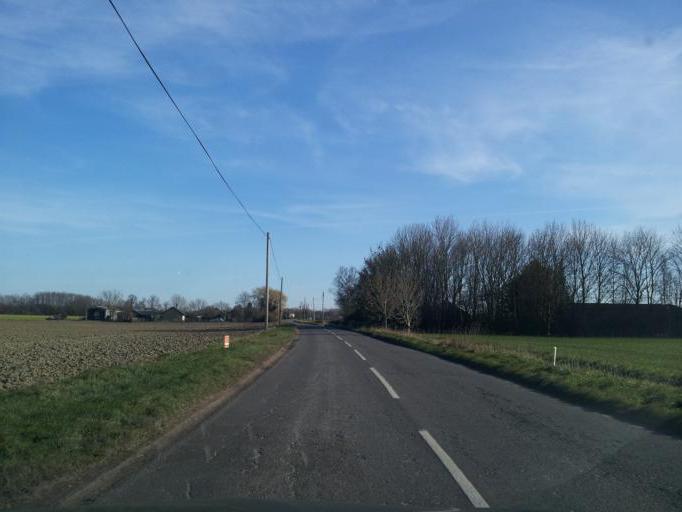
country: GB
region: England
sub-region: Cambridgeshire
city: Meldreth
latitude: 52.1198
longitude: 0.0240
